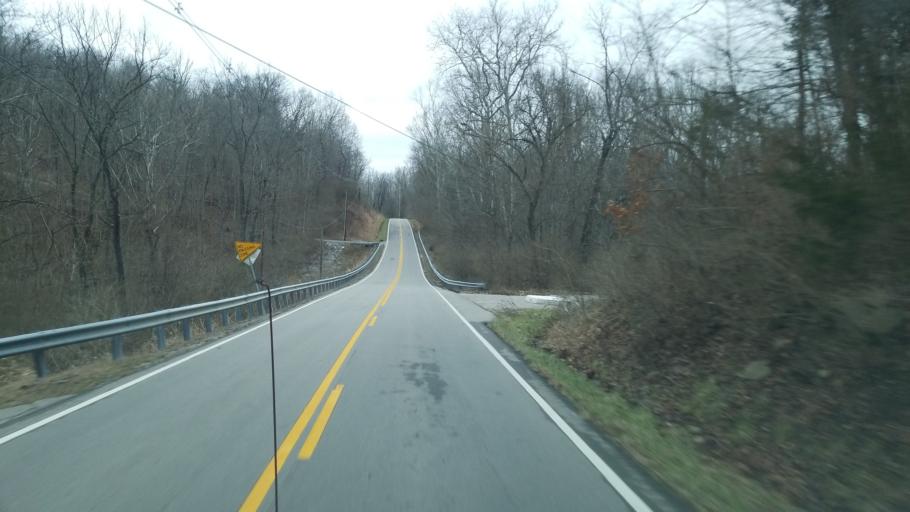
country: US
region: Ohio
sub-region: Clermont County
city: New Richmond
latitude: 38.8759
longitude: -84.2424
